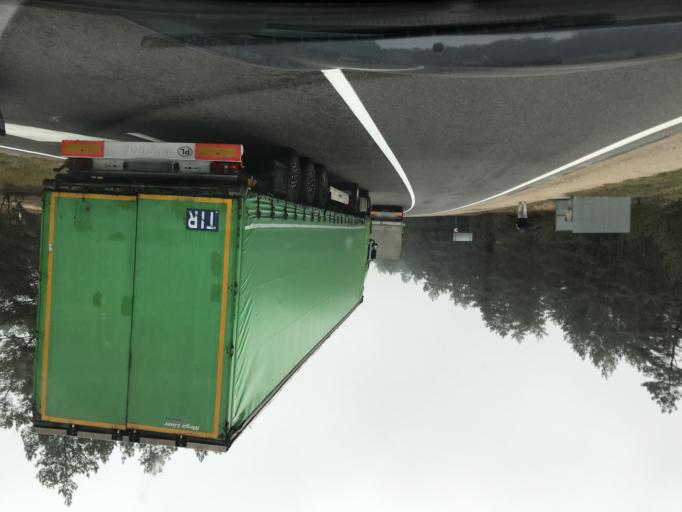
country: LT
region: Alytaus apskritis
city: Druskininkai
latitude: 53.9300
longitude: 23.9382
